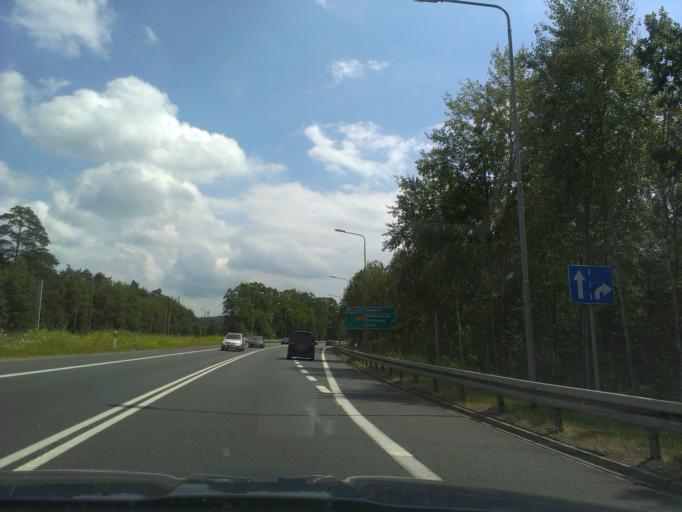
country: PL
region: West Pomeranian Voivodeship
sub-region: Powiat kamienski
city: Miedzyzdroje
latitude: 53.9148
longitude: 14.4211
